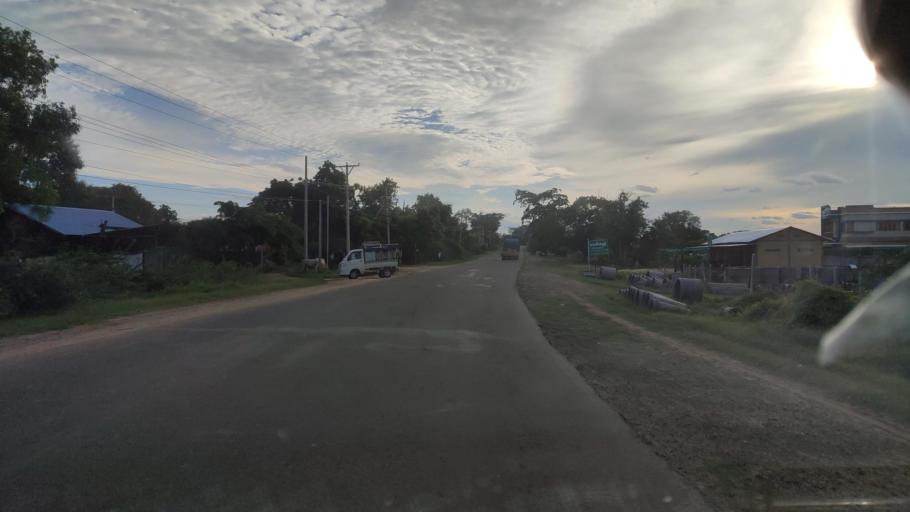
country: MM
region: Mandalay
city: Meiktila
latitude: 20.8479
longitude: 95.8119
